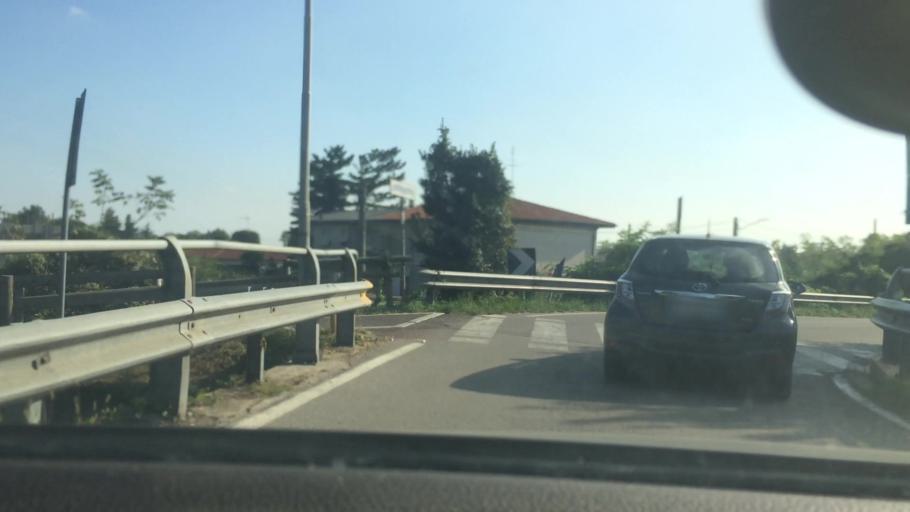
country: IT
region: Lombardy
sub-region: Citta metropolitana di Milano
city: Busto Garolfo
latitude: 45.5416
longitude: 8.8779
